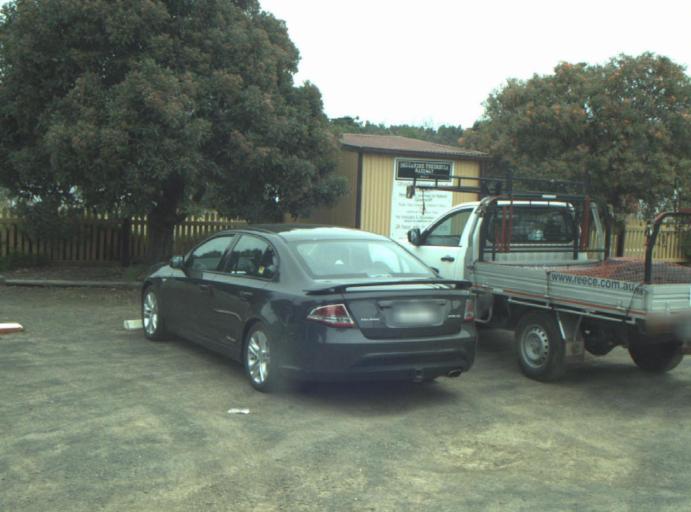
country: AU
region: Victoria
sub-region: Greater Geelong
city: Clifton Springs
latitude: -38.1798
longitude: 144.5574
